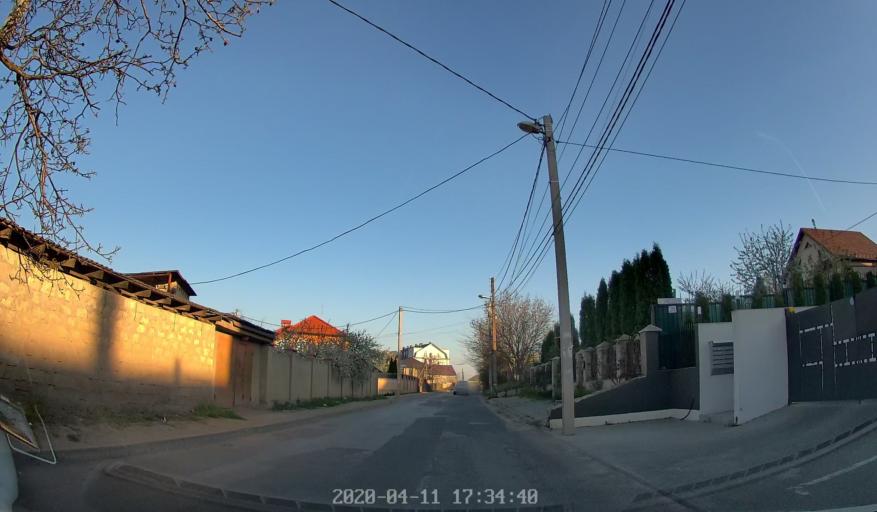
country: MD
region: Laloveni
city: Ialoveni
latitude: 46.9942
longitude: 28.8014
